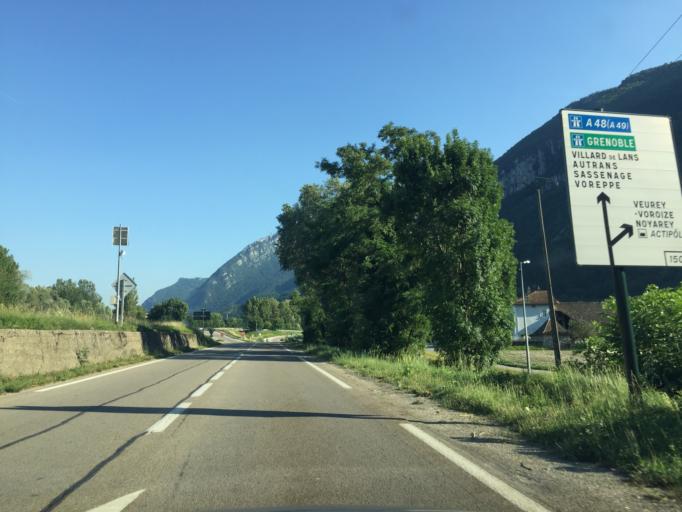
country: FR
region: Rhone-Alpes
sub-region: Departement de l'Isere
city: Veurey-Voroize
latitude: 45.2736
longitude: 5.6188
